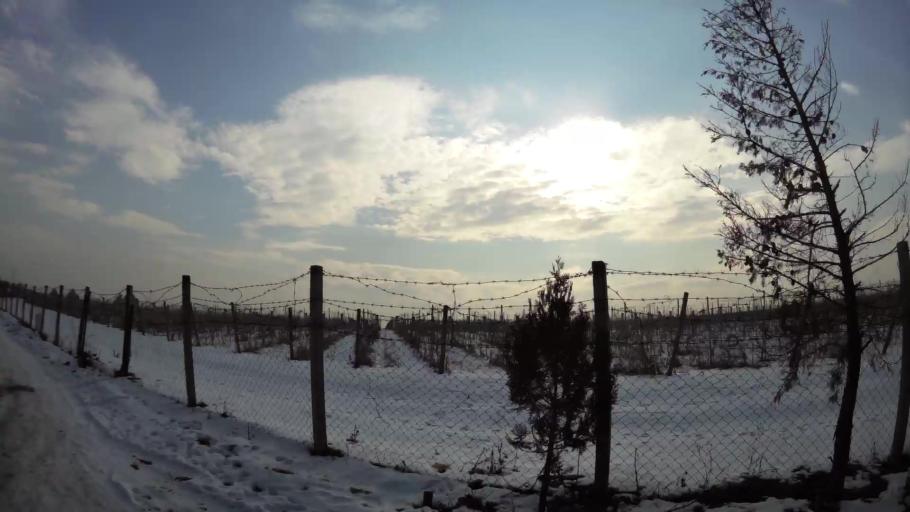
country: MK
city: Creshevo
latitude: 42.0100
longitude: 21.4957
